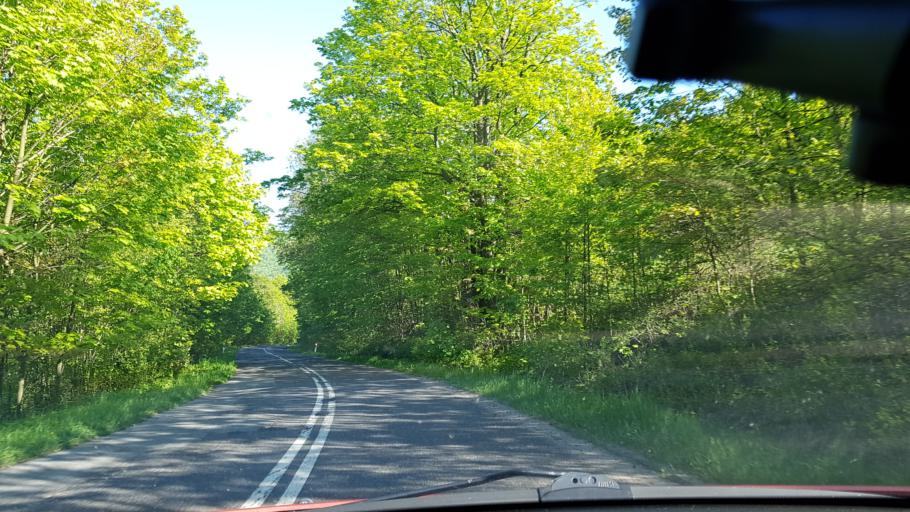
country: PL
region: Lower Silesian Voivodeship
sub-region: Powiat klodzki
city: Bozkow
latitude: 50.5717
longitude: 16.6087
